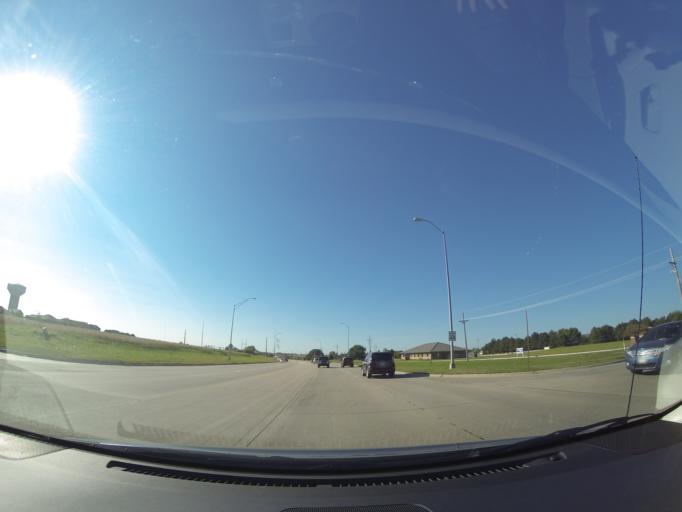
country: US
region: Nebraska
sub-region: Sarpy County
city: Gretna
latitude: 41.1284
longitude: -96.2531
